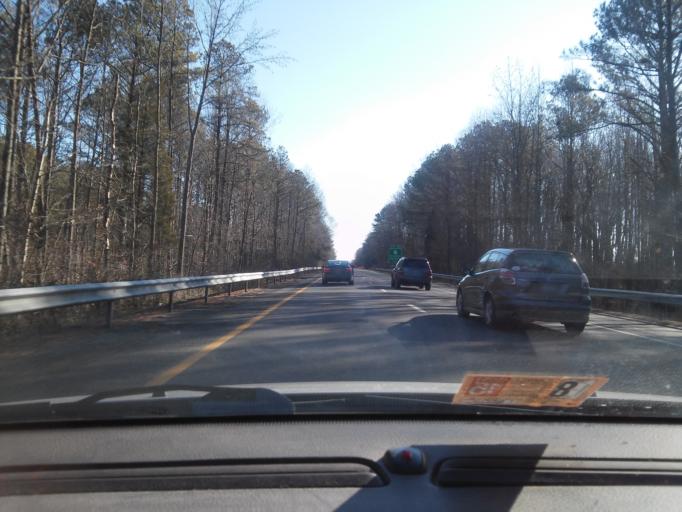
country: US
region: Virginia
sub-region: Henrico County
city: Wyndham
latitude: 37.6897
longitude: -77.6916
